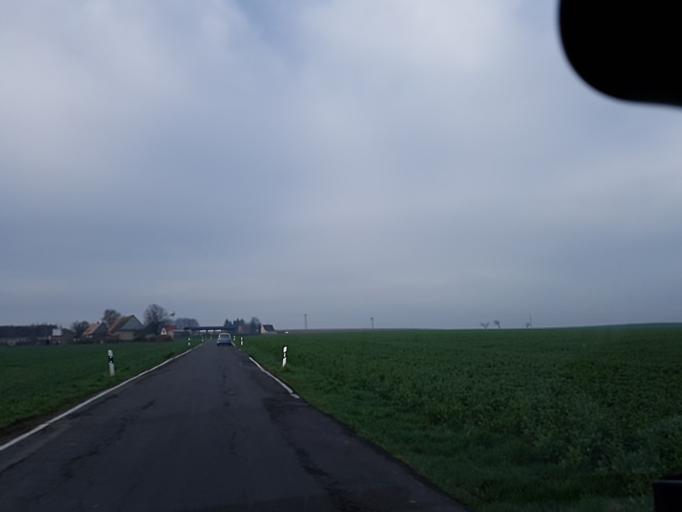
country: DE
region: Saxony
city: Naundorf
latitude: 51.2367
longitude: 13.1275
